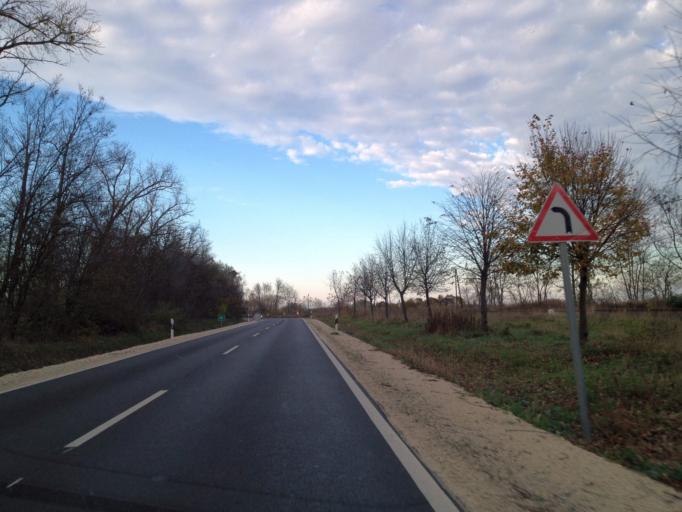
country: HU
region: Gyor-Moson-Sopron
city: Nyul
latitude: 47.6028
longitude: 17.6877
